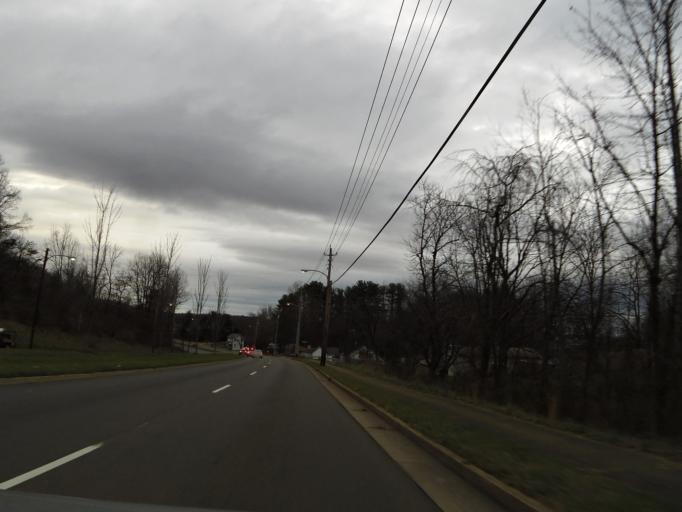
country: US
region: Tennessee
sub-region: Washington County
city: Johnson City
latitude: 36.3019
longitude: -82.3553
